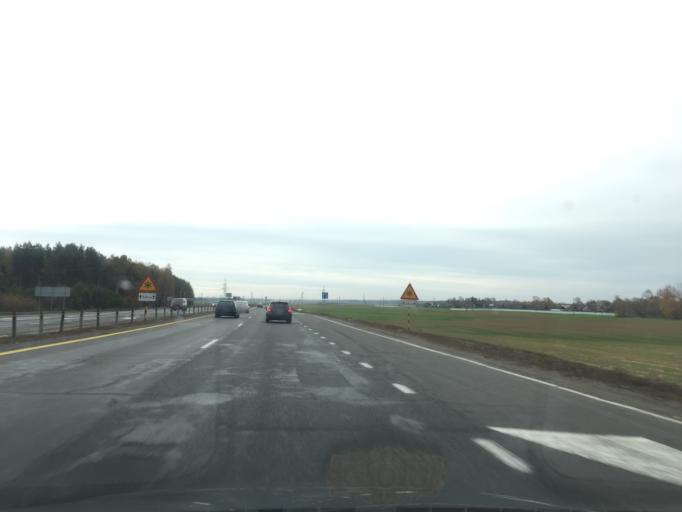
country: BY
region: Gomel
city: Horad Rechytsa
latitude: 52.3328
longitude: 30.5433
